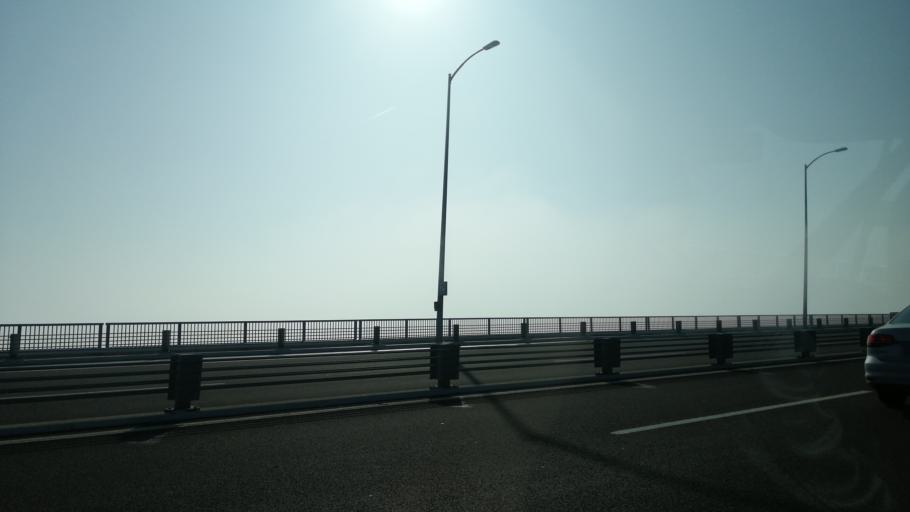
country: TR
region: Yalova
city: Altinova
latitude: 40.7394
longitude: 29.5132
